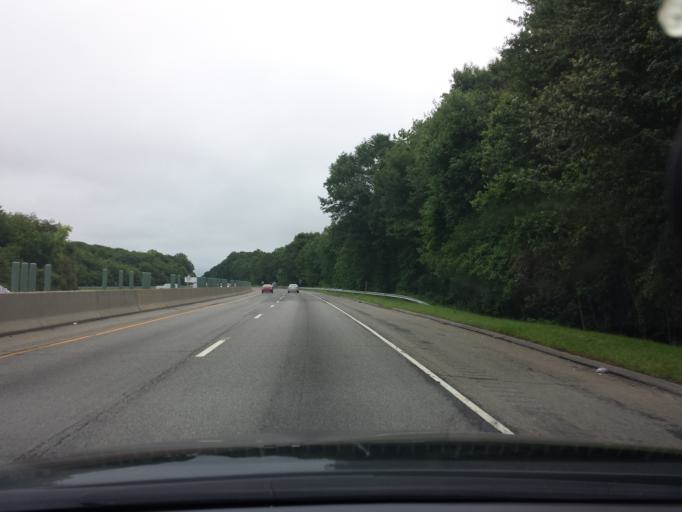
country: US
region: Connecticut
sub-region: Middlesex County
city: Saybrook Manor
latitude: 41.2906
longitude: -72.4190
